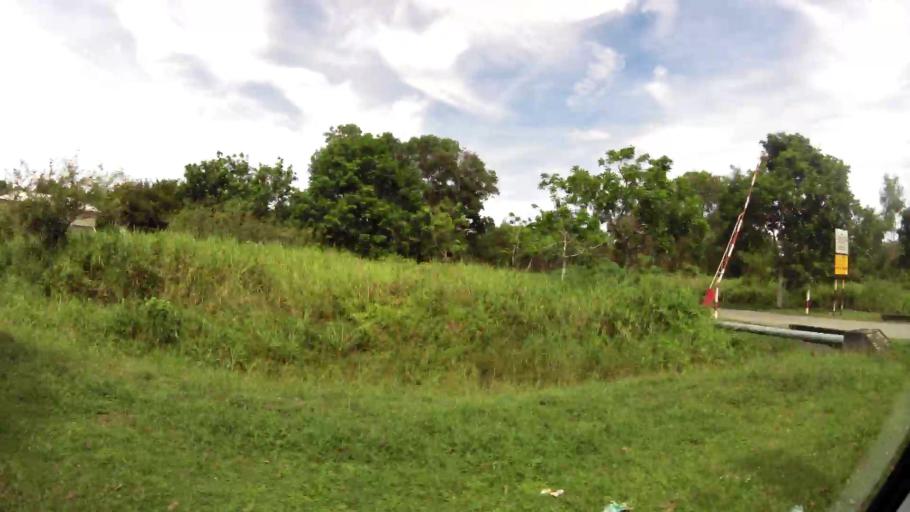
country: BN
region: Belait
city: Seria
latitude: 4.6012
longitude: 114.3101
